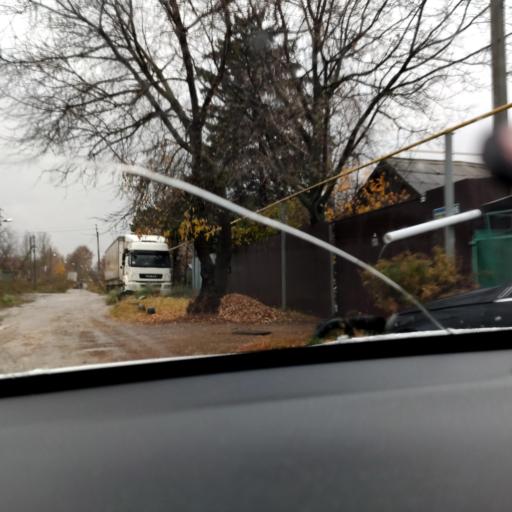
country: RU
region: Tatarstan
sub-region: Gorod Kazan'
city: Kazan
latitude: 55.8680
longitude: 49.1090
